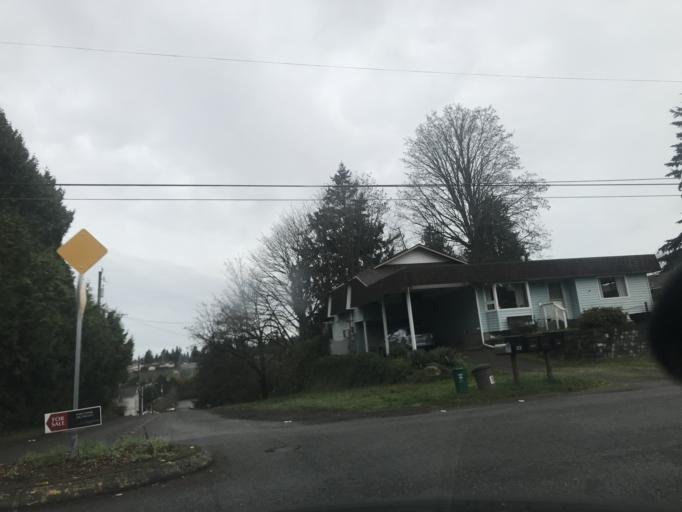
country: US
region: Washington
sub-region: King County
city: White Center
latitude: 47.5265
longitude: -122.3617
